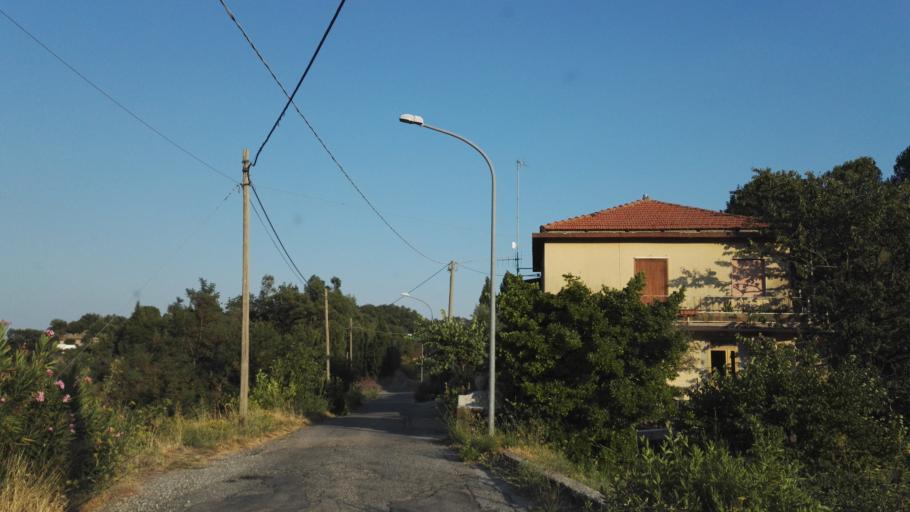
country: IT
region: Calabria
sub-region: Provincia di Reggio Calabria
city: Caulonia
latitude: 38.4058
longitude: 16.3636
